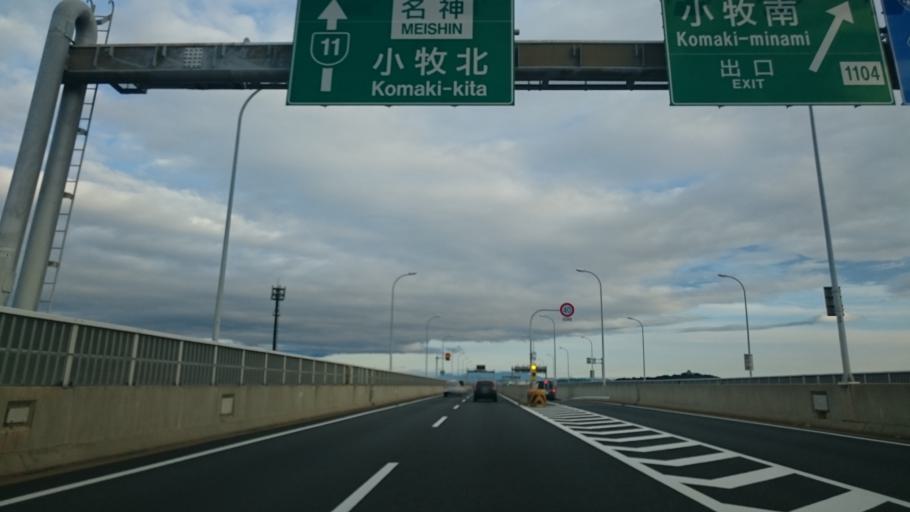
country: JP
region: Aichi
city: Komaki
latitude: 35.2691
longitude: 136.9074
